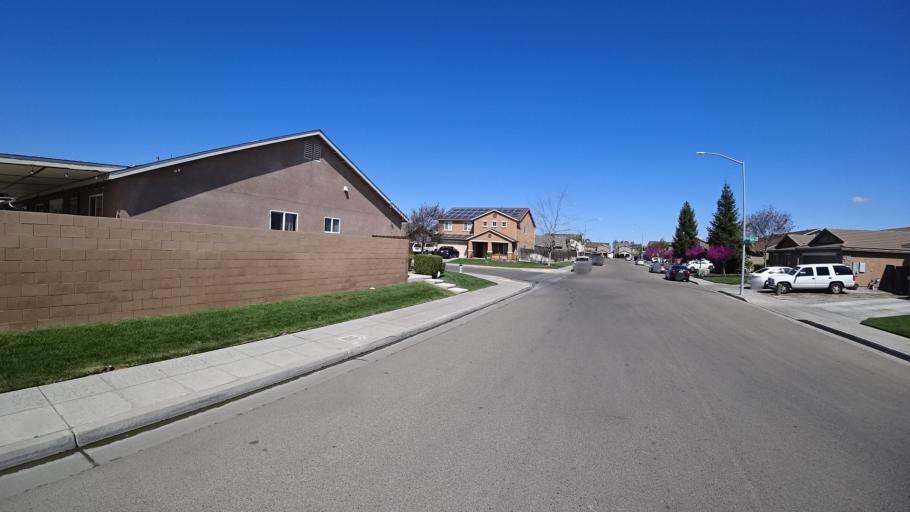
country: US
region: California
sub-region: Fresno County
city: West Park
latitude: 36.7834
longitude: -119.8949
